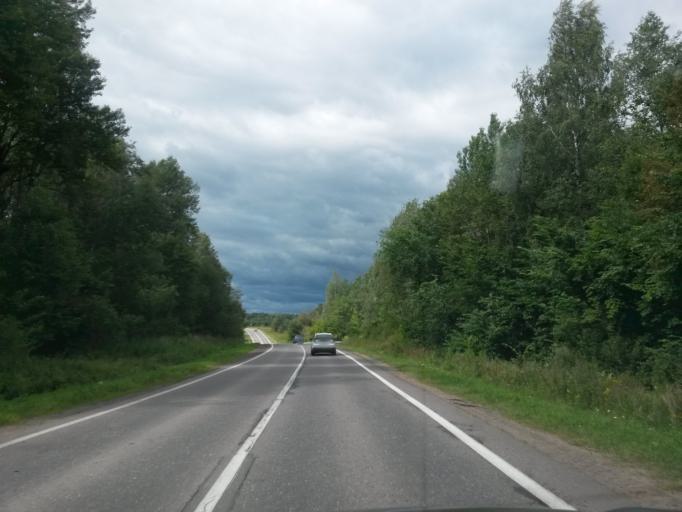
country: RU
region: Jaroslavl
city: Yaroslavl
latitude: 57.8016
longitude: 39.8245
